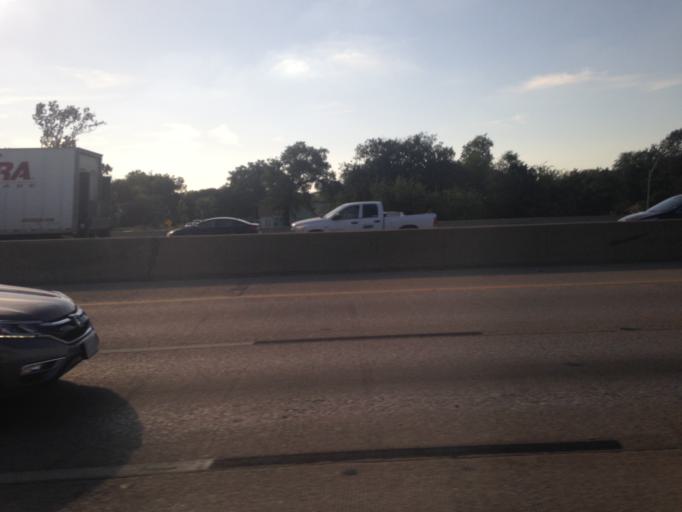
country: US
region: Texas
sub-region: Tarrant County
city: Fort Worth
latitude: 32.7162
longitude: -97.3204
